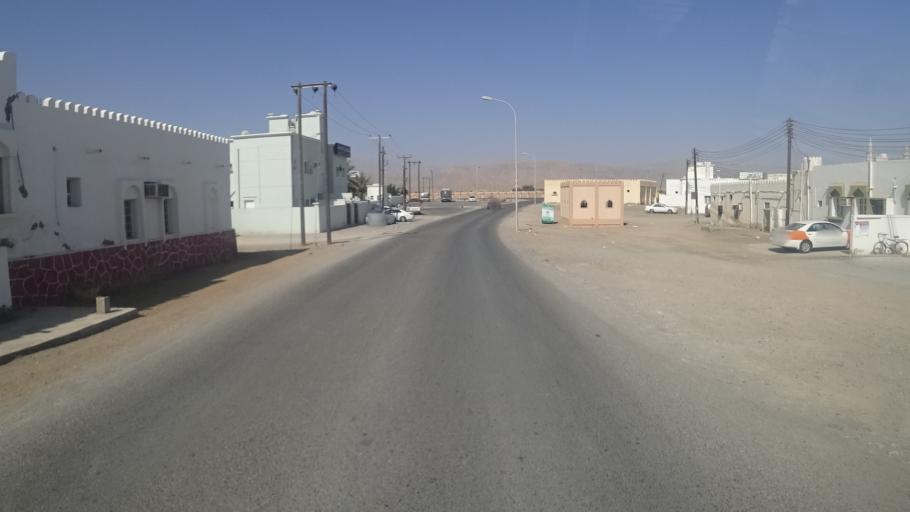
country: OM
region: Ash Sharqiyah
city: Sur
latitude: 22.5407
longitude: 59.4842
